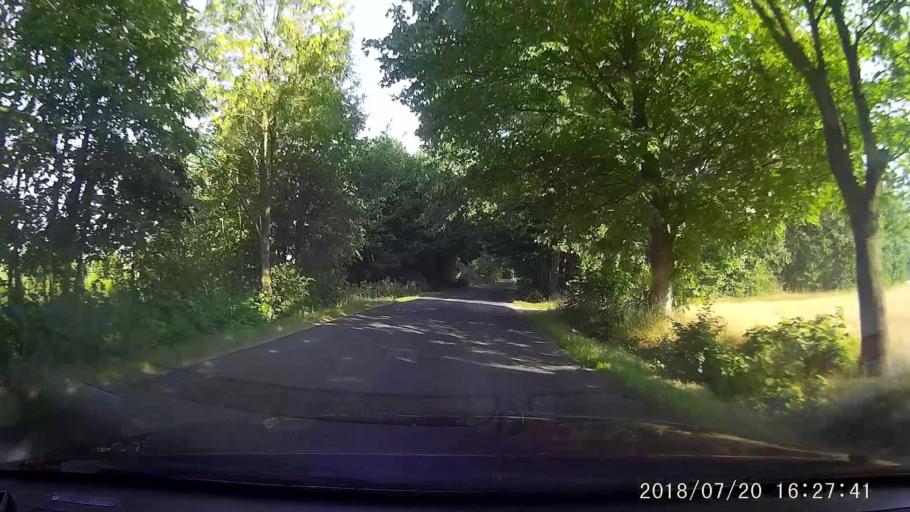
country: PL
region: Lower Silesian Voivodeship
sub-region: Powiat zgorzelecki
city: Lagow
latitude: 51.1242
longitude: 15.0483
